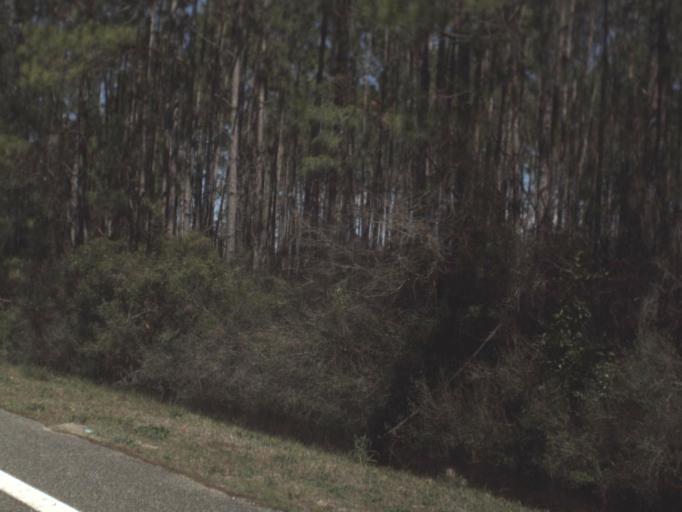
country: US
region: Florida
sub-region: Gulf County
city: Port Saint Joe
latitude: 29.7755
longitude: -85.2682
